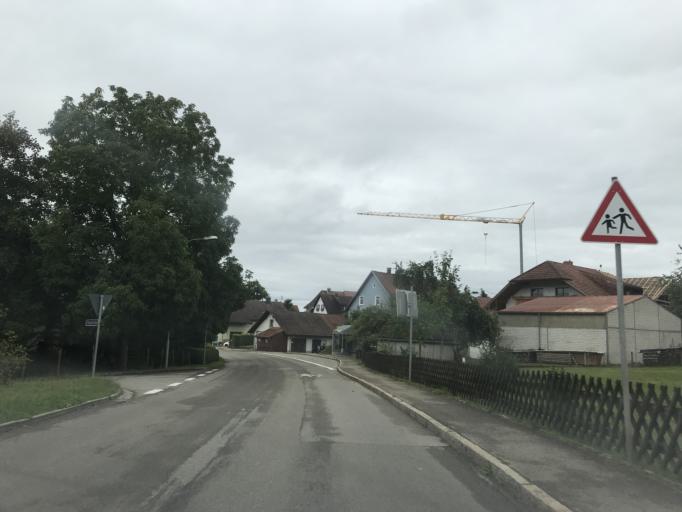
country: DE
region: Baden-Wuerttemberg
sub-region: Freiburg Region
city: Murg
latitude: 47.5833
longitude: 8.0320
